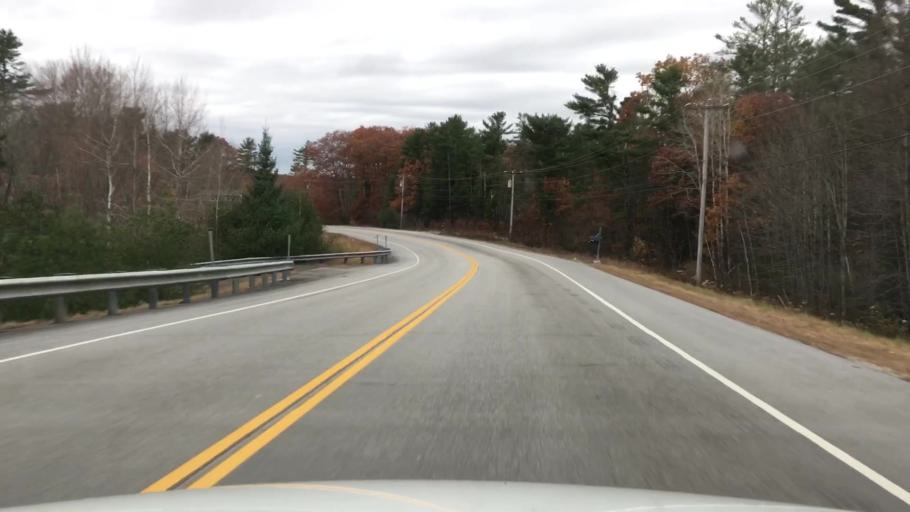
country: US
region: Maine
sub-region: Hancock County
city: Orland
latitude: 44.5569
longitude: -68.6979
